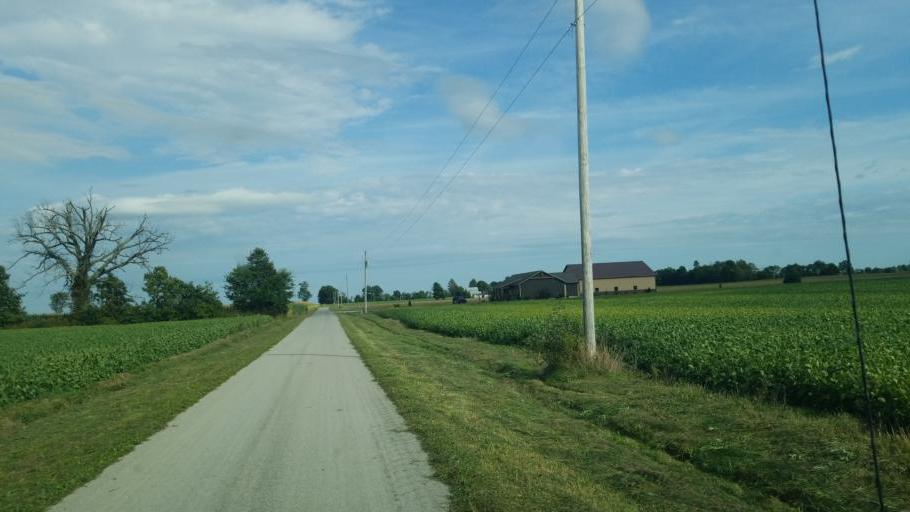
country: US
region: Ohio
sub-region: Hardin County
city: Forest
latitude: 40.8544
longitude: -83.5123
